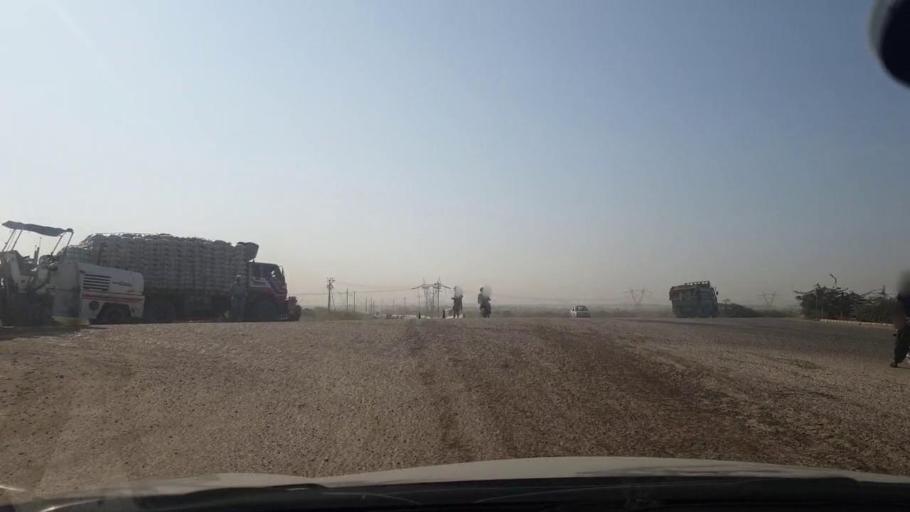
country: PK
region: Sindh
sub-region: Karachi District
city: Karachi
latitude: 25.0749
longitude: 67.0138
